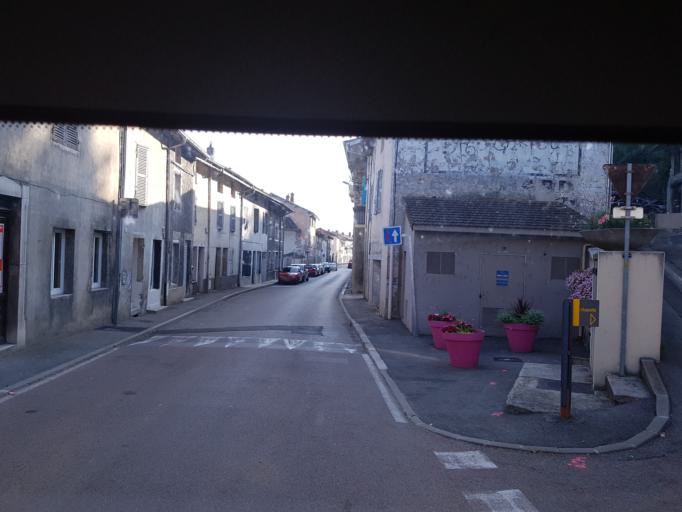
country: FR
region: Rhone-Alpes
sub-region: Departement de l'Ain
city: Neuville-sur-Ain
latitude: 46.0508
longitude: 5.3439
